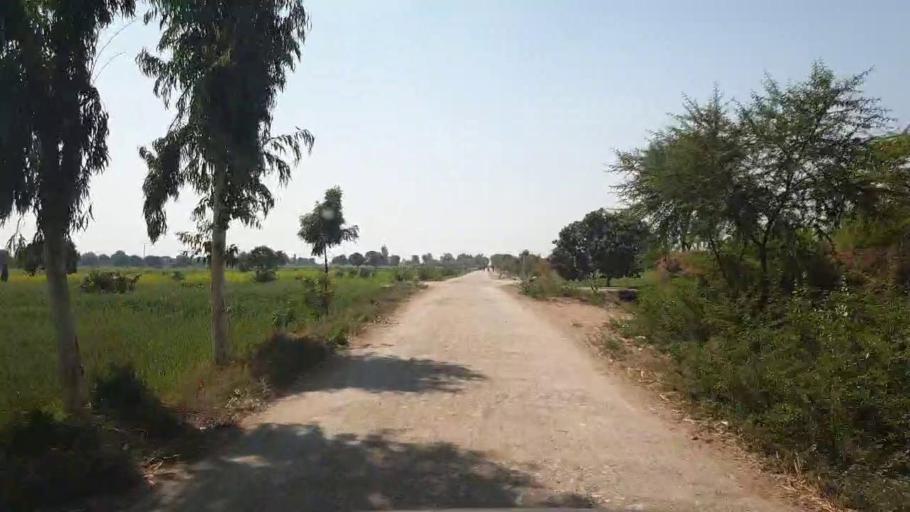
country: PK
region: Sindh
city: Digri
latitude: 25.2446
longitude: 69.2285
